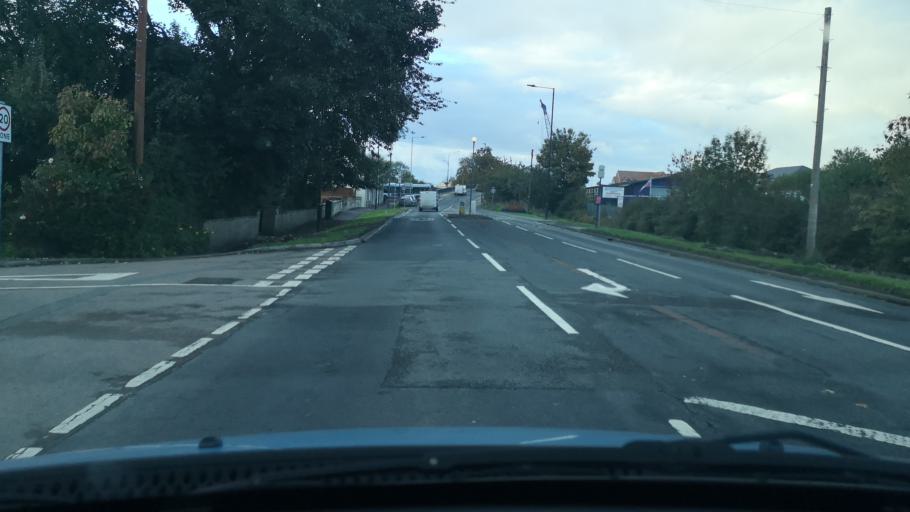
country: GB
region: England
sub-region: Doncaster
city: Hatfield
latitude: 53.6061
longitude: -0.9644
